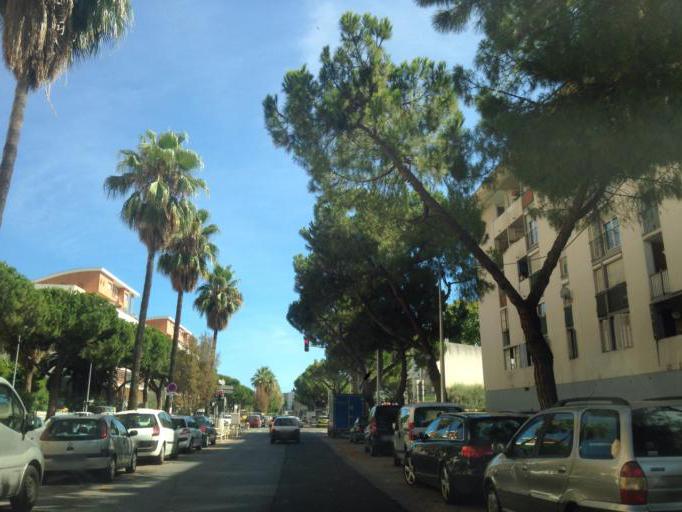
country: FR
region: Provence-Alpes-Cote d'Azur
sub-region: Departement des Alpes-Maritimes
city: Saint-Laurent-du-Var
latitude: 43.6743
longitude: 7.2079
